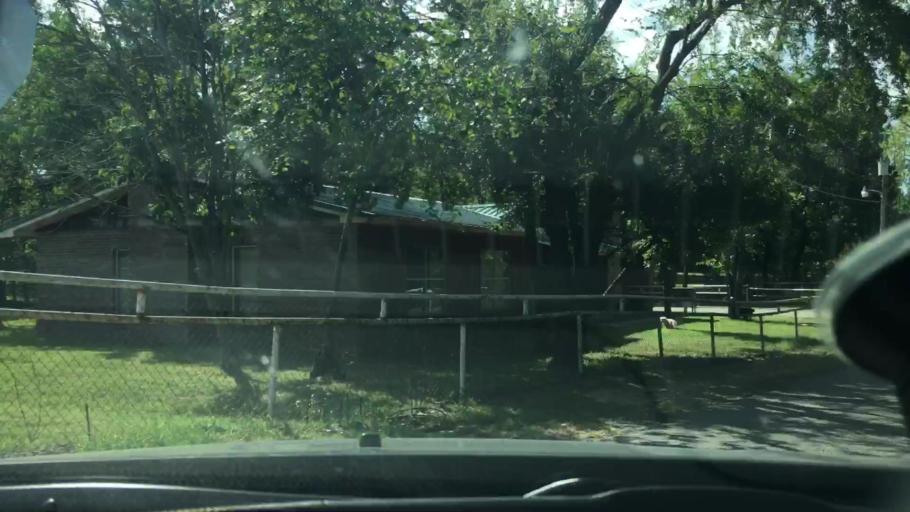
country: US
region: Oklahoma
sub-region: Carter County
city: Ardmore
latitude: 34.1435
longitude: -97.0818
